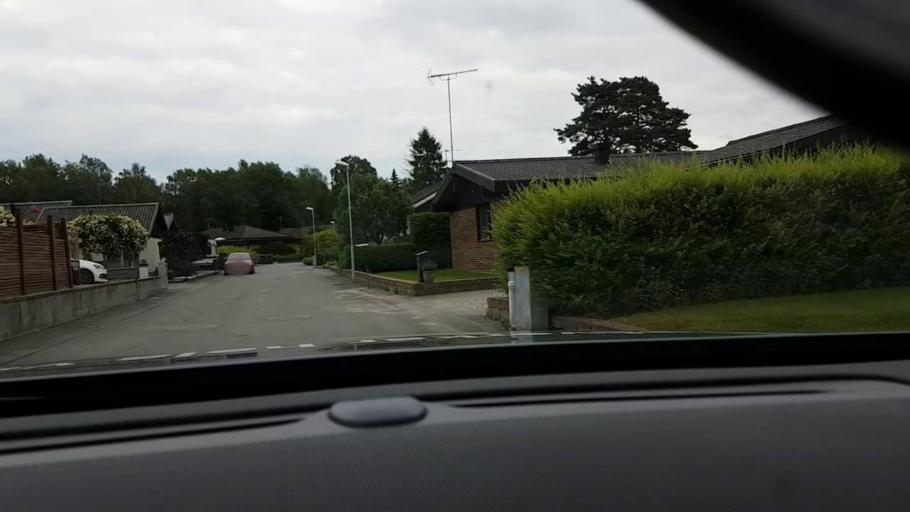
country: SE
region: Skane
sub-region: Hassleholms Kommun
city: Hassleholm
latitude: 56.1729
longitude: 13.8001
